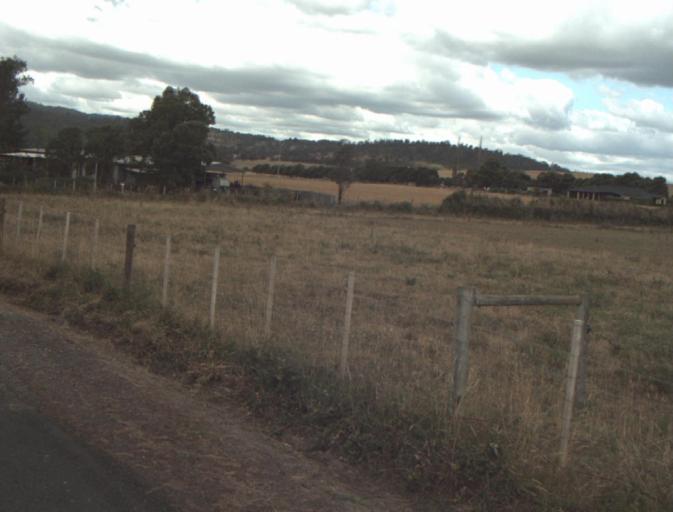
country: AU
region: Tasmania
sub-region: Launceston
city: Mayfield
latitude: -41.2866
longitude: 146.9979
